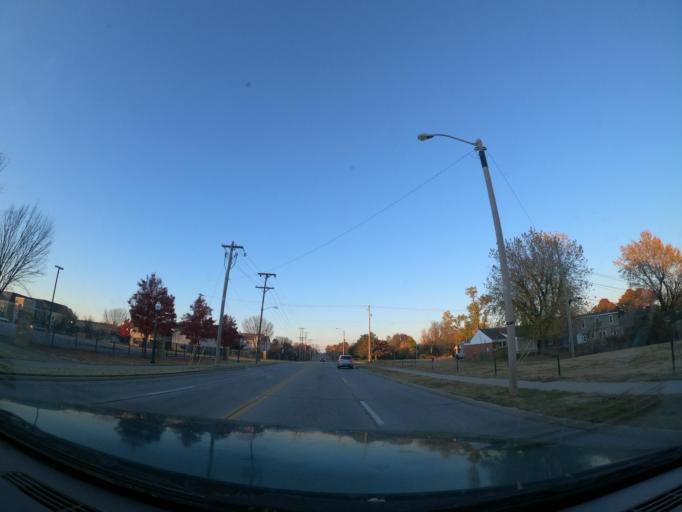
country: US
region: Oklahoma
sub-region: Tulsa County
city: Tulsa
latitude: 36.1522
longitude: -95.9403
